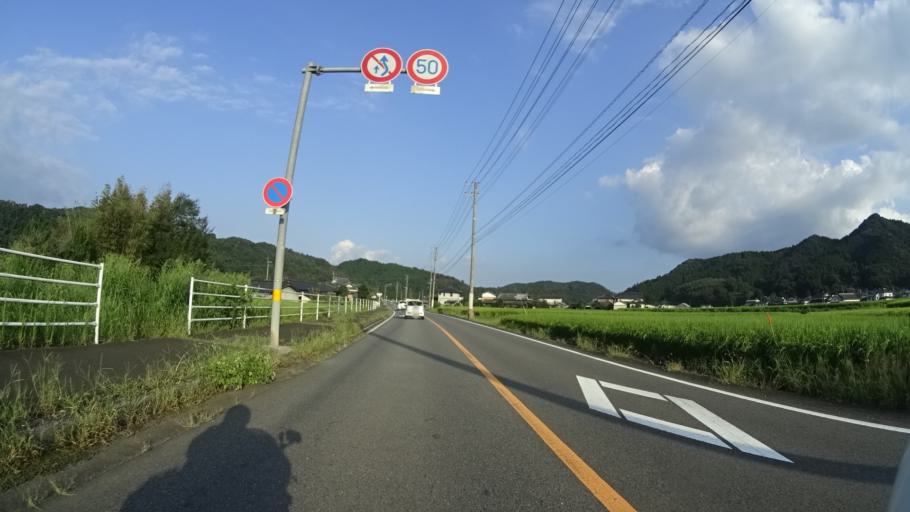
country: JP
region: Oita
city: Bungo-Takada-shi
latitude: 33.4353
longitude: 131.3648
